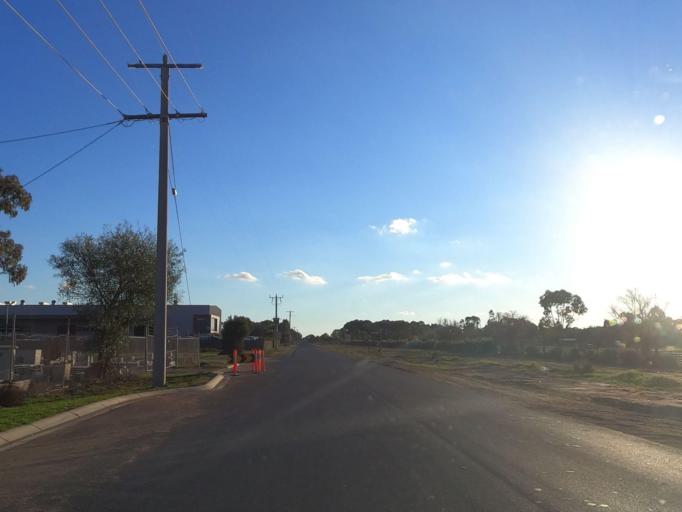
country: AU
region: Victoria
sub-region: Swan Hill
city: Swan Hill
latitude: -35.3254
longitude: 143.5360
